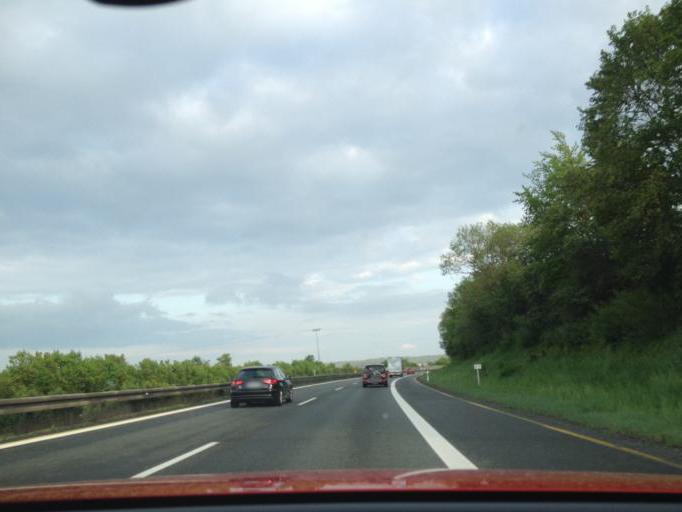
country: DE
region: Bavaria
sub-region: Upper Palatinate
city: Weiden
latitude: 49.6654
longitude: 12.1402
